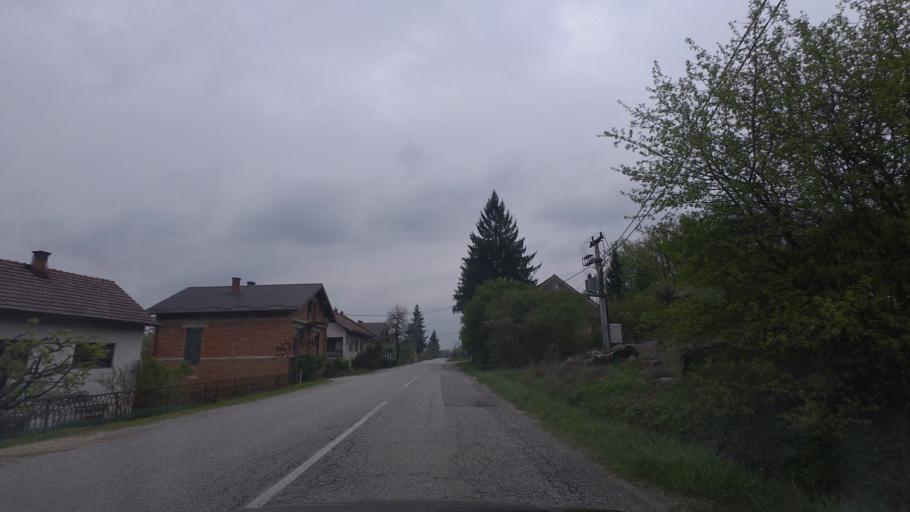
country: HR
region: Karlovacka
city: Ozalj
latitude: 45.6358
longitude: 15.5407
